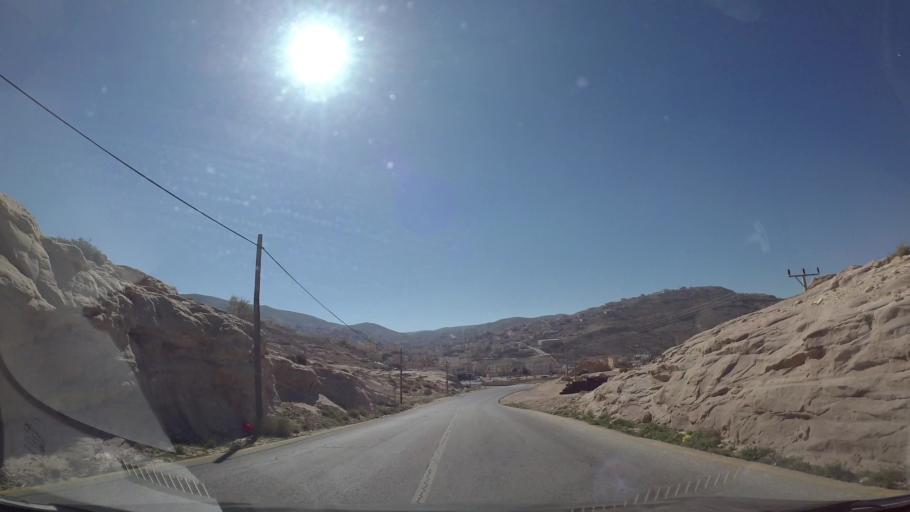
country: JO
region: Ma'an
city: Petra
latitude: 30.3307
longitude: 35.4690
